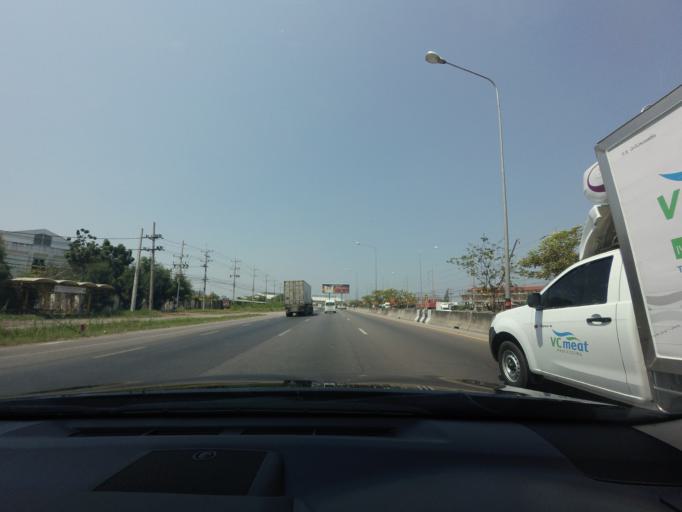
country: TH
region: Samut Sakhon
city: Ban Phaeo
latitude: 13.5080
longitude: 100.1325
